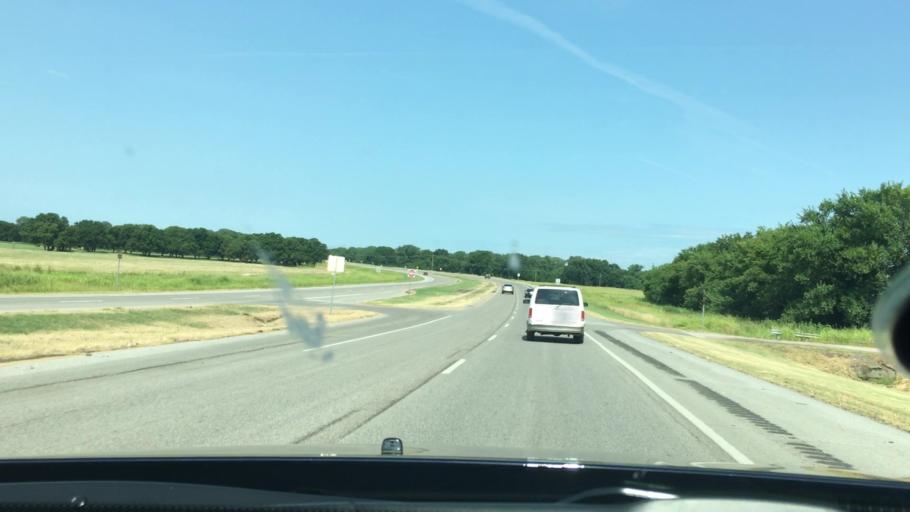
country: US
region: Oklahoma
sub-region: Murray County
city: Davis
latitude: 34.5034
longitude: -97.1303
